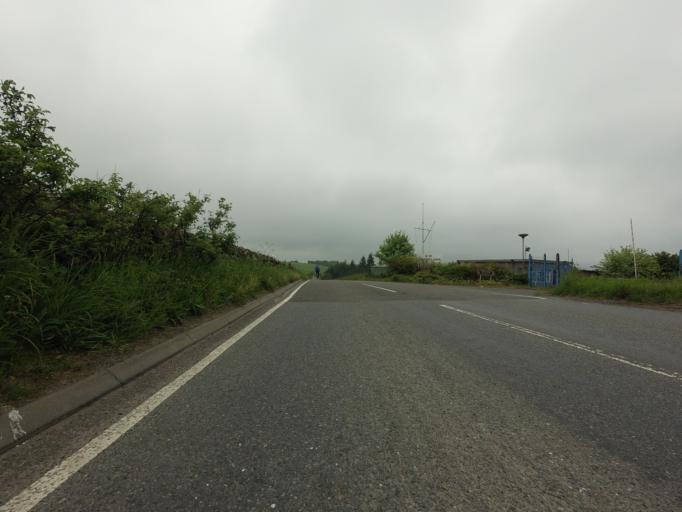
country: GB
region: Scotland
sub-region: Fife
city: Townhill
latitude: 56.1142
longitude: -3.4477
